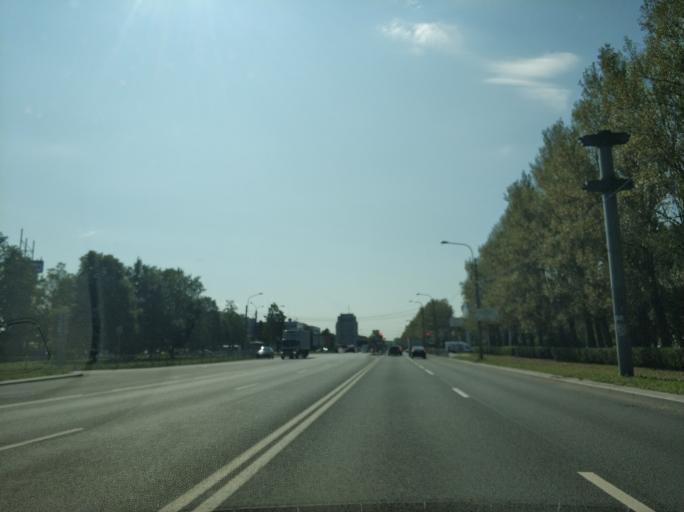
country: RU
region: St.-Petersburg
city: Kupchino
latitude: 59.8536
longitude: 30.3374
